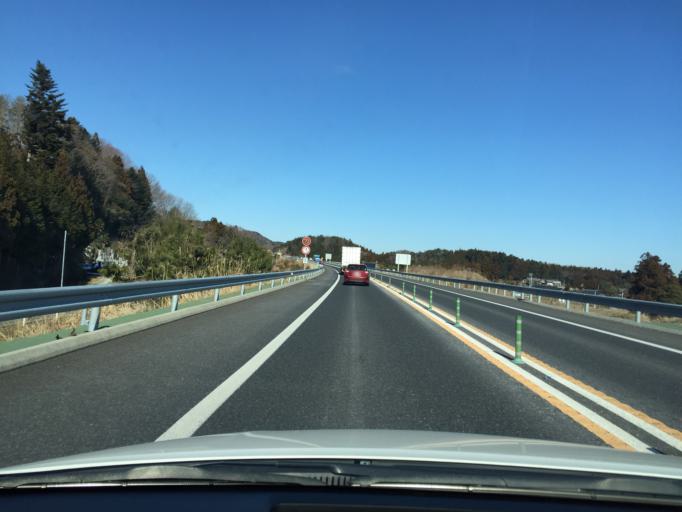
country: JP
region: Miyagi
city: Marumori
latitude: 37.7278
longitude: 140.9158
